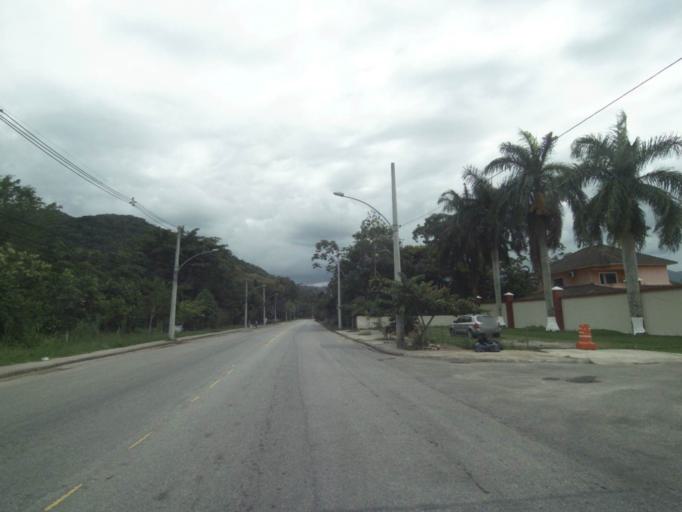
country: BR
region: Rio de Janeiro
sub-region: Nilopolis
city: Nilopolis
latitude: -23.0049
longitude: -43.5107
